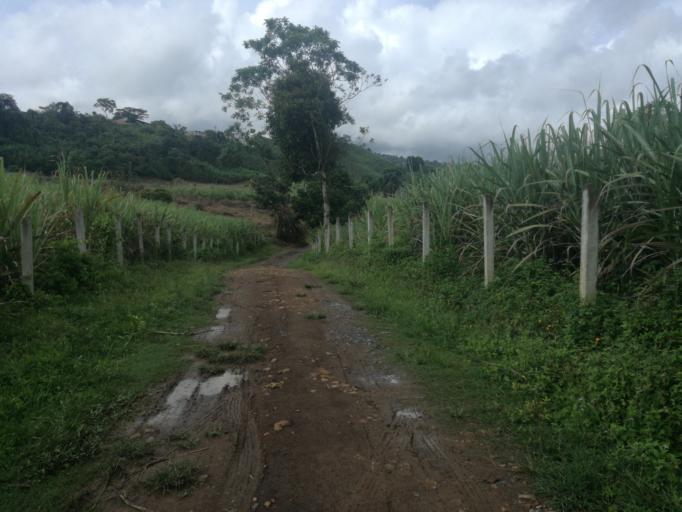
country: CO
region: Boyaca
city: Santana
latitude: 6.0634
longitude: -73.4857
